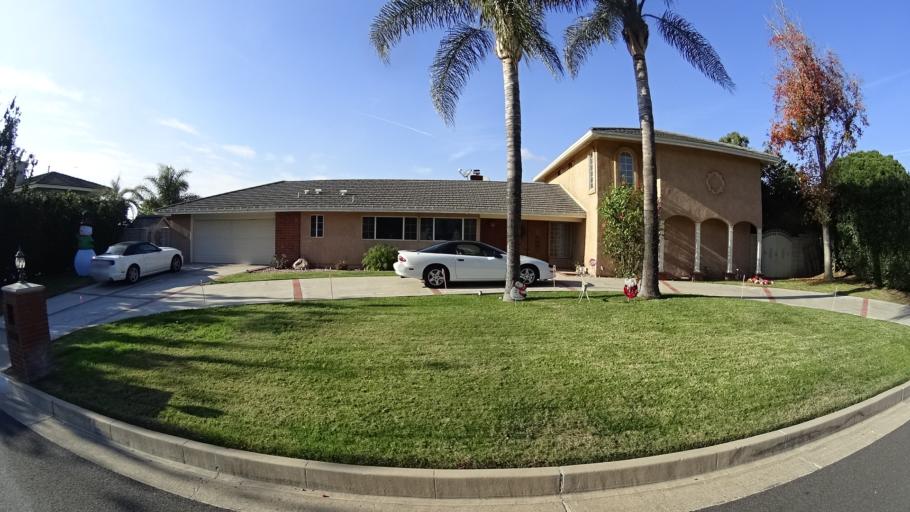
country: US
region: California
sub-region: Orange County
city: North Tustin
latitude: 33.7603
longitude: -117.7909
